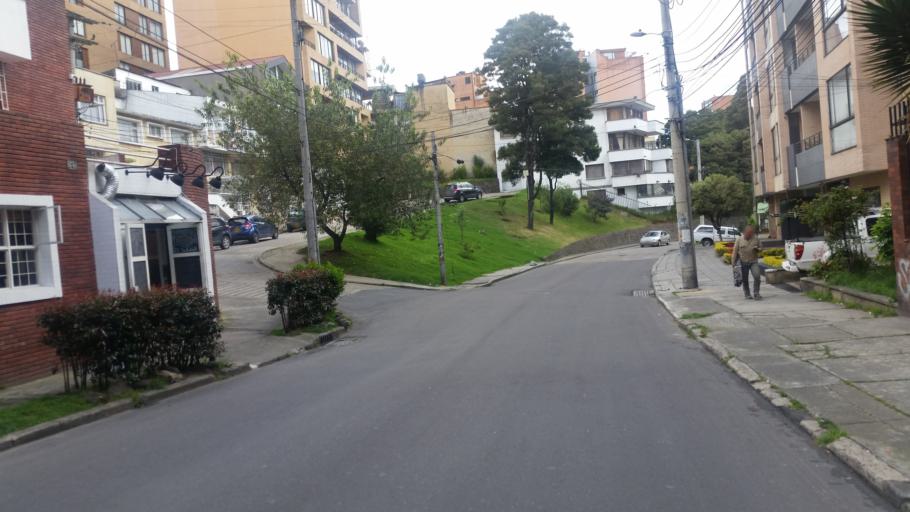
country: CO
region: Bogota D.C.
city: Bogota
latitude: 4.6381
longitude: -74.0618
